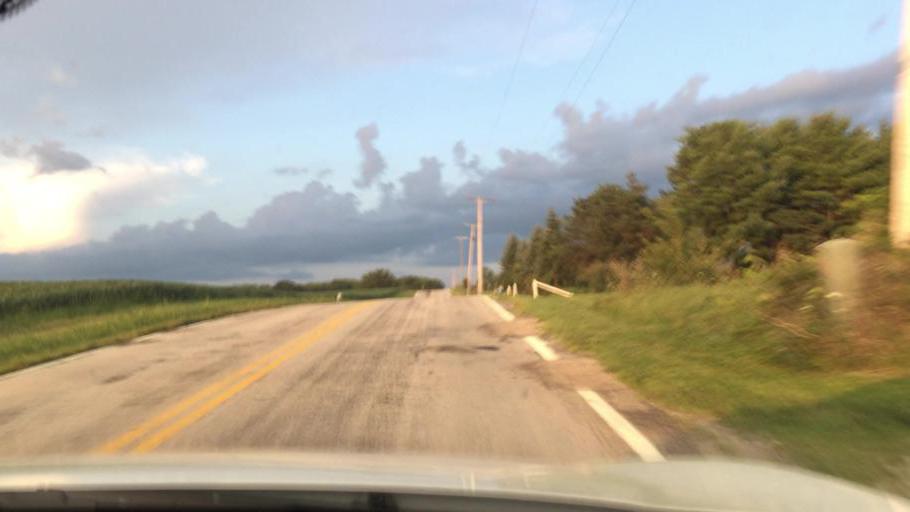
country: US
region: Ohio
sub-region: Champaign County
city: Mechanicsburg
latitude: 40.0093
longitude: -83.5970
